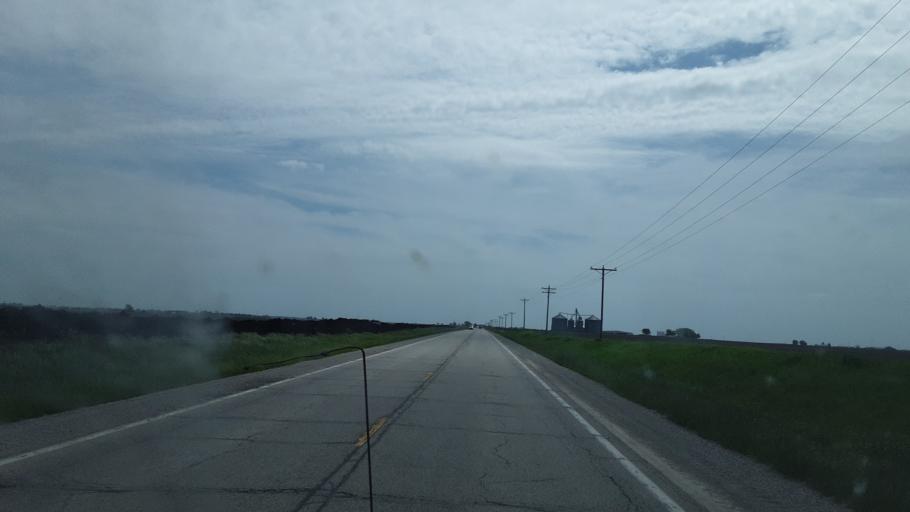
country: US
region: Illinois
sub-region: Logan County
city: Atlanta
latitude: 40.3116
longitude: -89.1467
